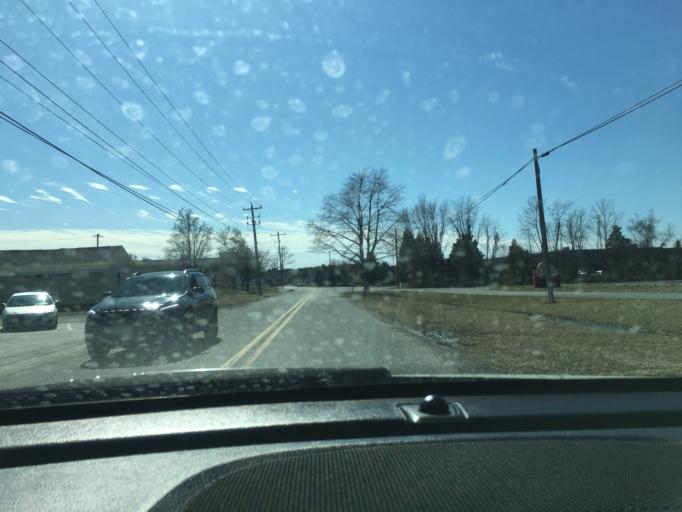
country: US
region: Maryland
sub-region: Wicomico County
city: Delmar
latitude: 38.4050
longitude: -75.5707
